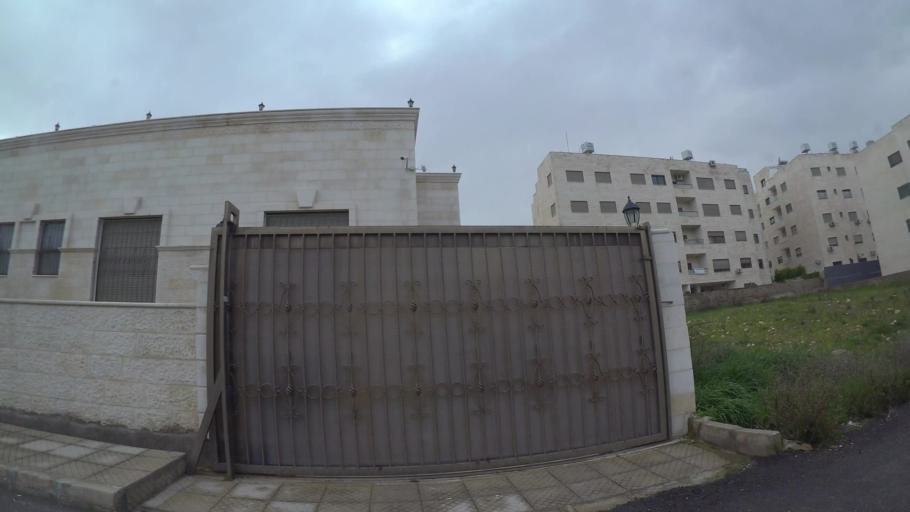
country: JO
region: Amman
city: Umm as Summaq
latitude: 31.9061
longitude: 35.8510
